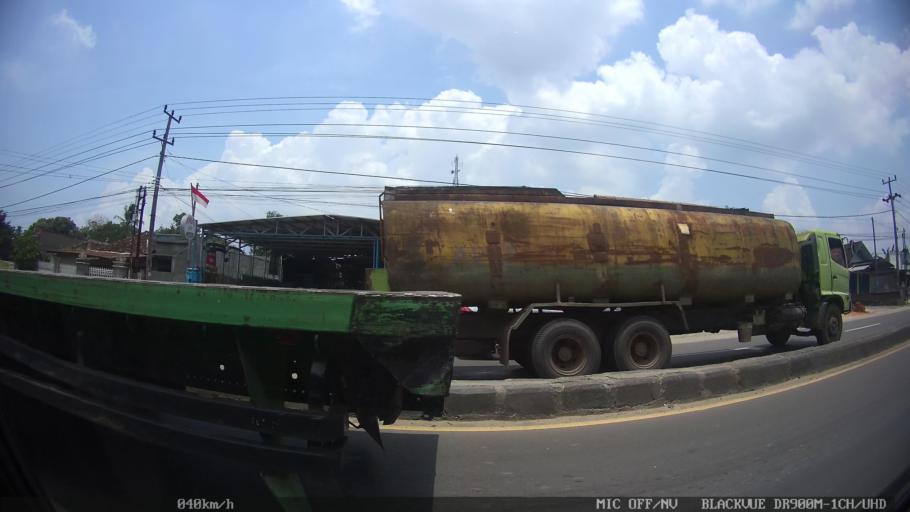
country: ID
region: Lampung
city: Natar
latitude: -5.3251
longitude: 105.2012
